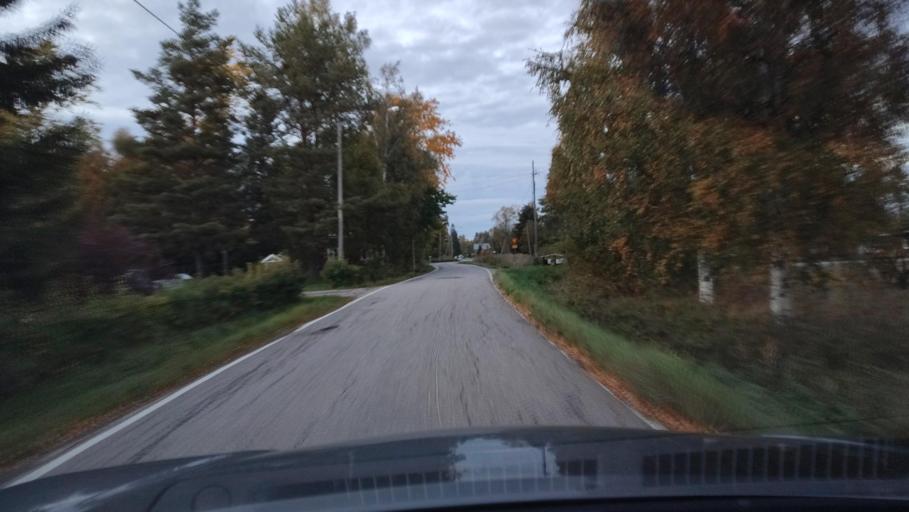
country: FI
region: Ostrobothnia
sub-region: Sydosterbotten
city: Kristinestad
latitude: 62.2582
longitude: 21.5078
